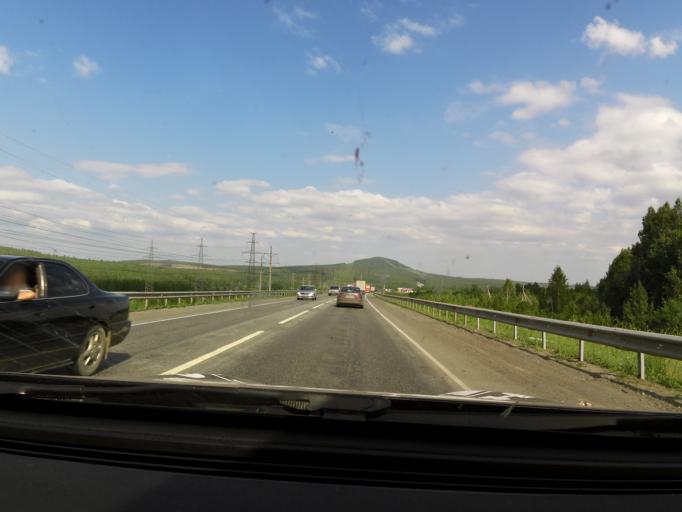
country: RU
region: Sverdlovsk
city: Revda
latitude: 56.8278
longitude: 59.9408
